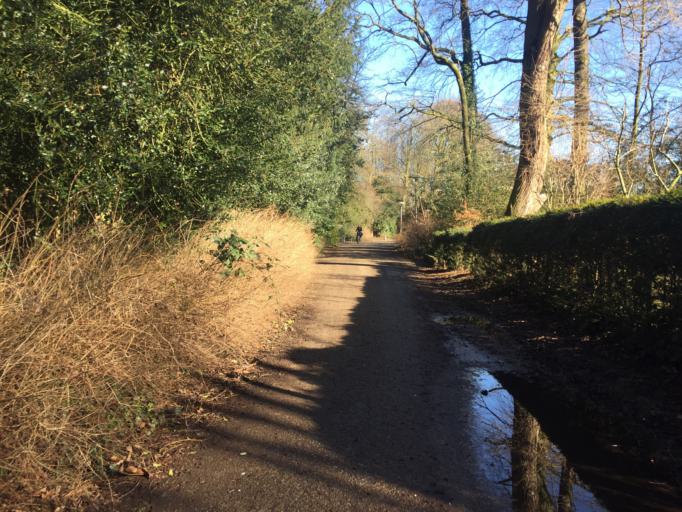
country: NL
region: Utrecht
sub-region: Gemeente Utrecht
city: Utrecht
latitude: 52.0861
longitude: 5.0915
